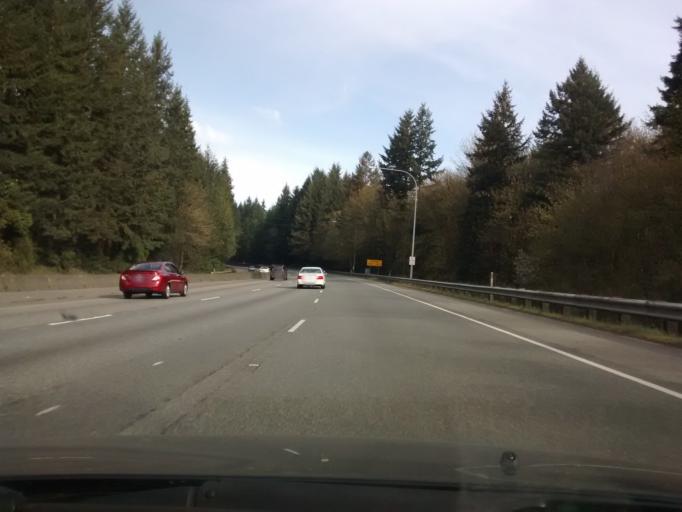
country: US
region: Washington
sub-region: Kitsap County
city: Navy Yard City
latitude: 47.5251
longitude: -122.6611
